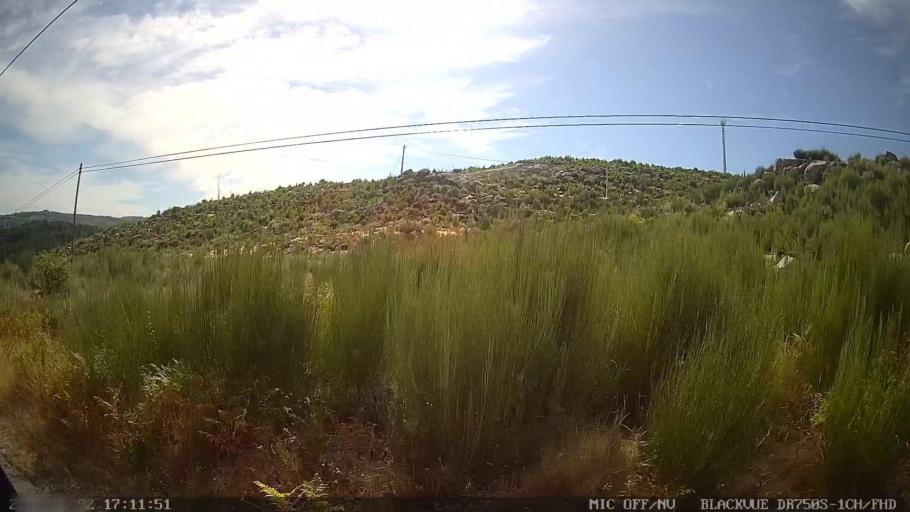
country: PT
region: Vila Real
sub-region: Sabrosa
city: Sabrosa
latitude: 41.3561
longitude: -7.5899
